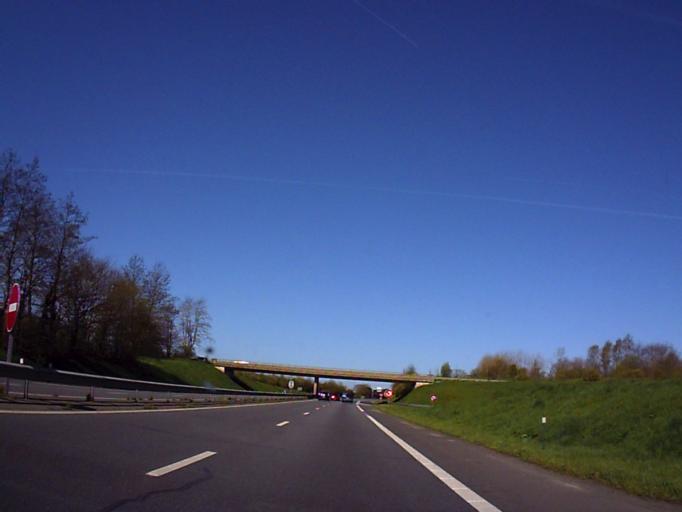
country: FR
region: Brittany
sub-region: Departement des Cotes-d'Armor
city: Plestan
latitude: 48.4182
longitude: -2.4403
